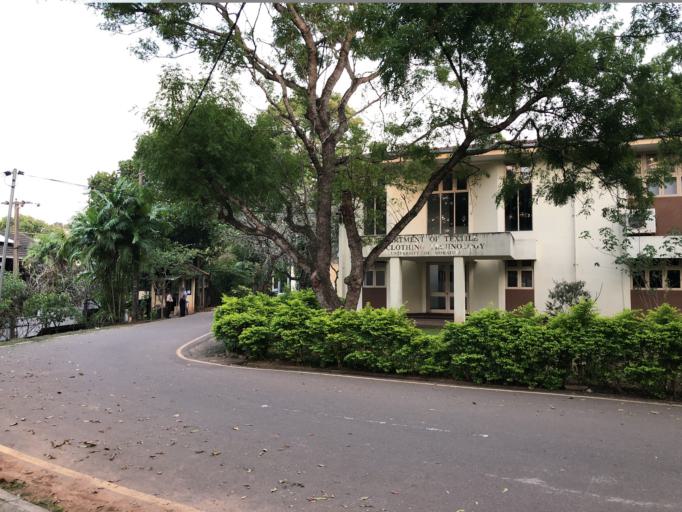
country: LK
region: Western
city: Moratuwa
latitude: 6.7984
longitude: 79.9011
